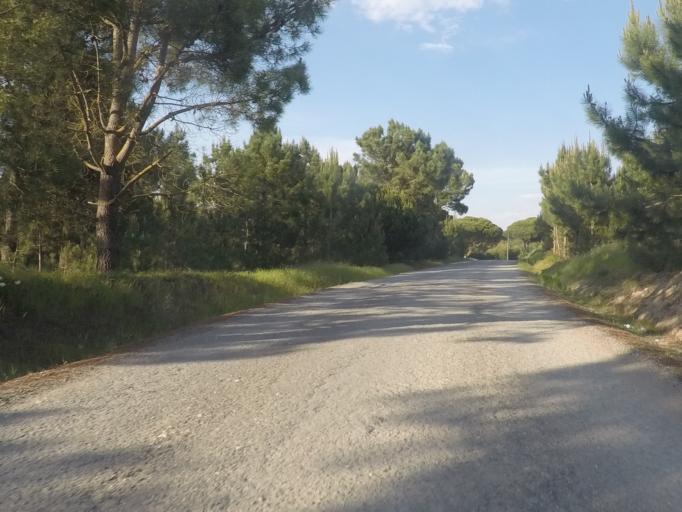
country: PT
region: Setubal
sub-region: Sesimbra
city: Sesimbra
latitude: 38.4590
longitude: -9.1862
